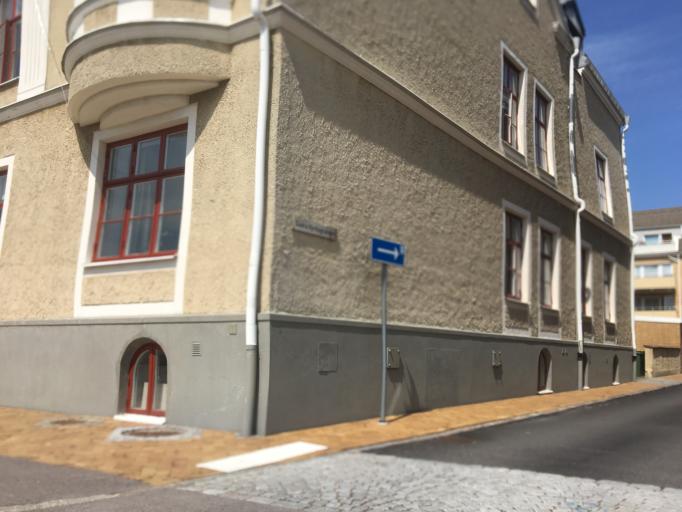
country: SE
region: Skane
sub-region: Landskrona
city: Landskrona
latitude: 55.8664
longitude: 12.8259
